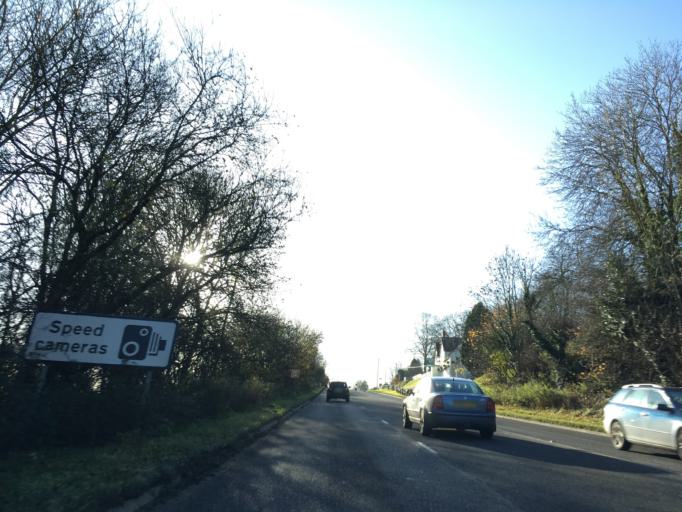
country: GB
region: England
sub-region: Borough of Swindon
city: Chiseldon
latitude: 51.5231
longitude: -1.7244
